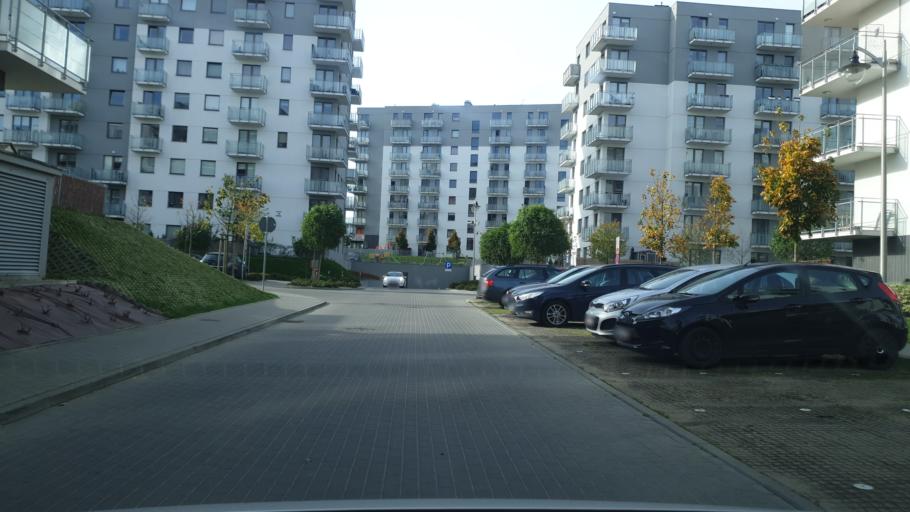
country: PL
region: Pomeranian Voivodeship
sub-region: Powiat gdanski
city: Kowale
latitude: 54.3499
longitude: 18.5887
